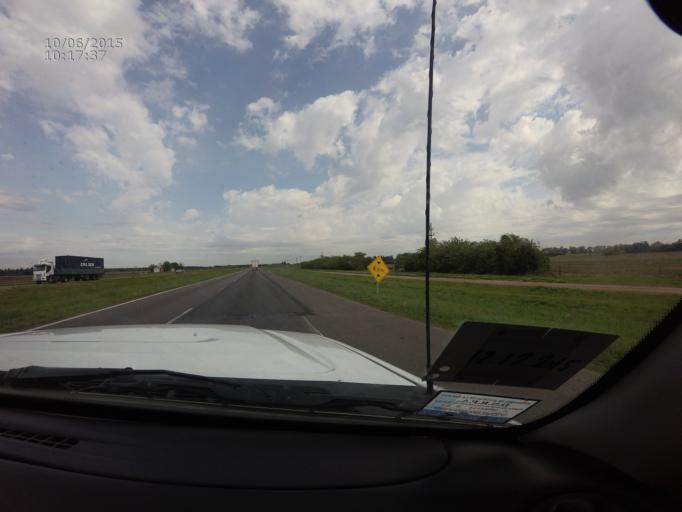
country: AR
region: Buenos Aires
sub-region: Partido de San Pedro
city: San Pedro
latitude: -33.7477
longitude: -59.7743
